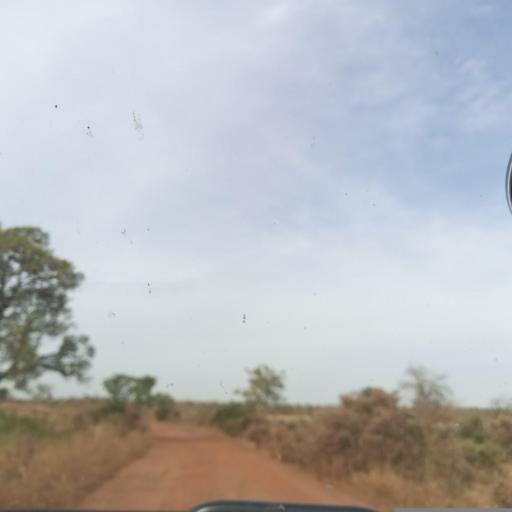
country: ML
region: Koulikoro
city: Koulikoro
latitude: 13.1082
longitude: -7.6215
